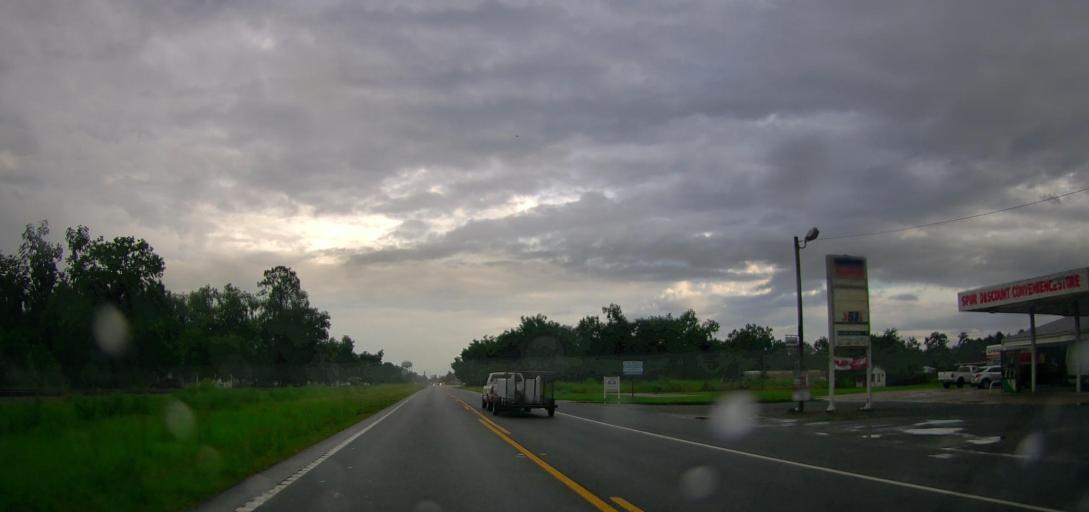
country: US
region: Georgia
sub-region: Ware County
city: Deenwood
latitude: 31.2398
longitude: -82.3717
